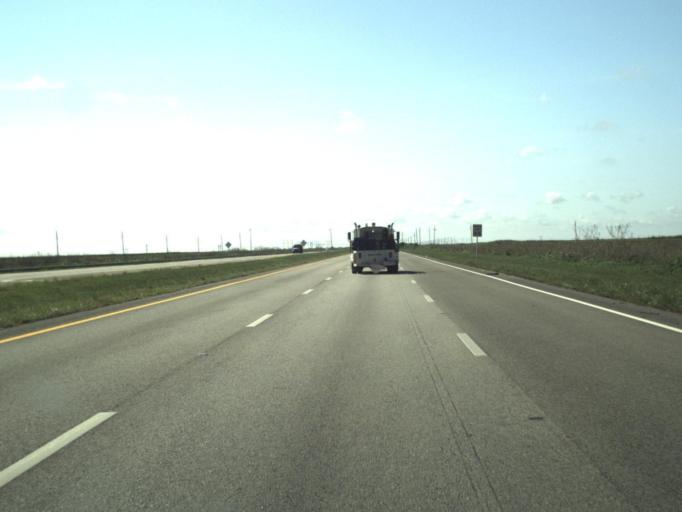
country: US
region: Florida
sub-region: Broward County
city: Coral Springs
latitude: 26.3691
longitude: -80.5645
